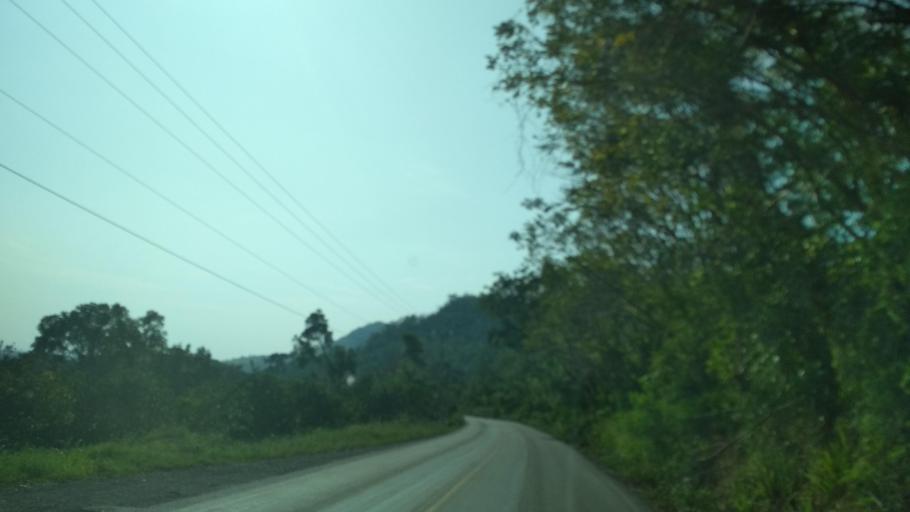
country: MX
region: Veracruz
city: Agua Dulce
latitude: 20.3991
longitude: -97.2611
